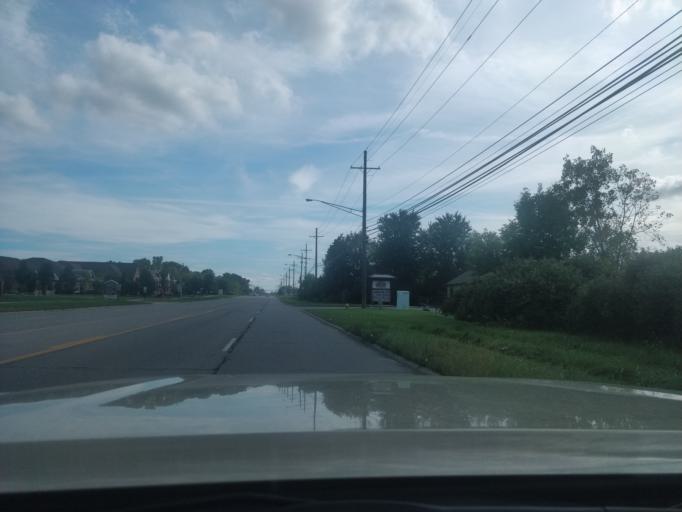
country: US
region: Michigan
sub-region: Wayne County
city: Woodhaven
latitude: 42.1610
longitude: -83.2270
